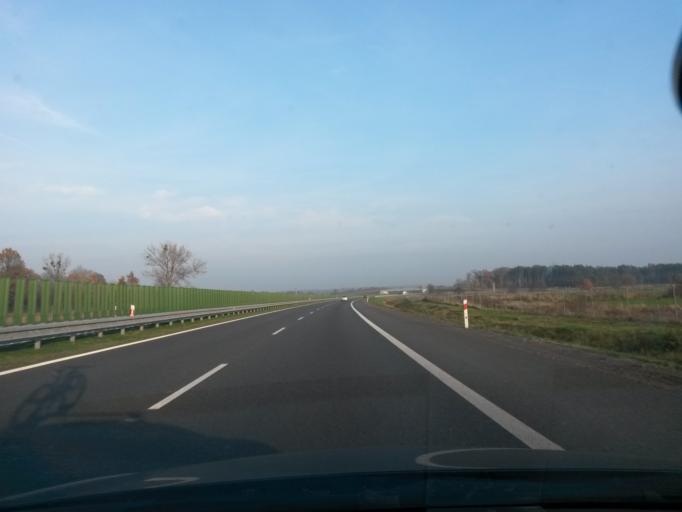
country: PL
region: Lower Silesian Voivodeship
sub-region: Powiat olesnicki
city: Miedzyborz
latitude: 51.3036
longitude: 17.5977
